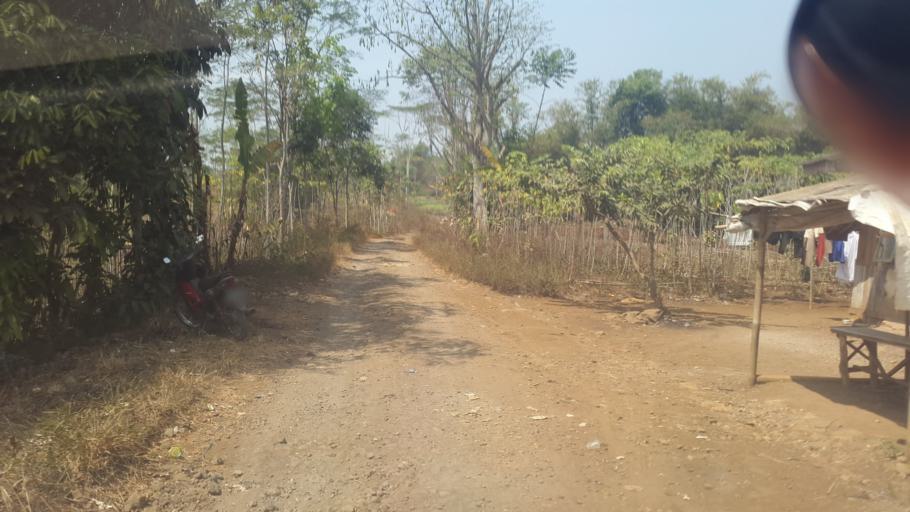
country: ID
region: West Java
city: Ciroyom
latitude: -7.0973
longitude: 106.8277
